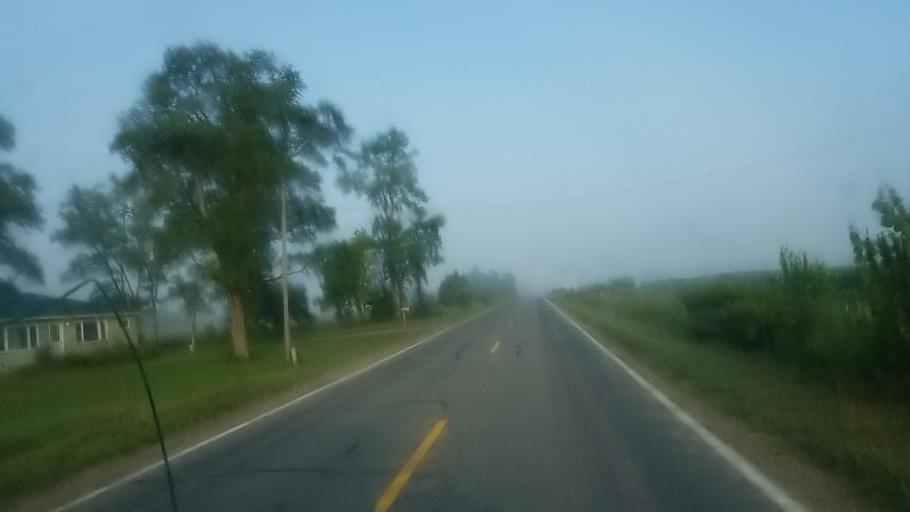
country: US
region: Michigan
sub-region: Newaygo County
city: Fremont
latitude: 43.4678
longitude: -86.0698
